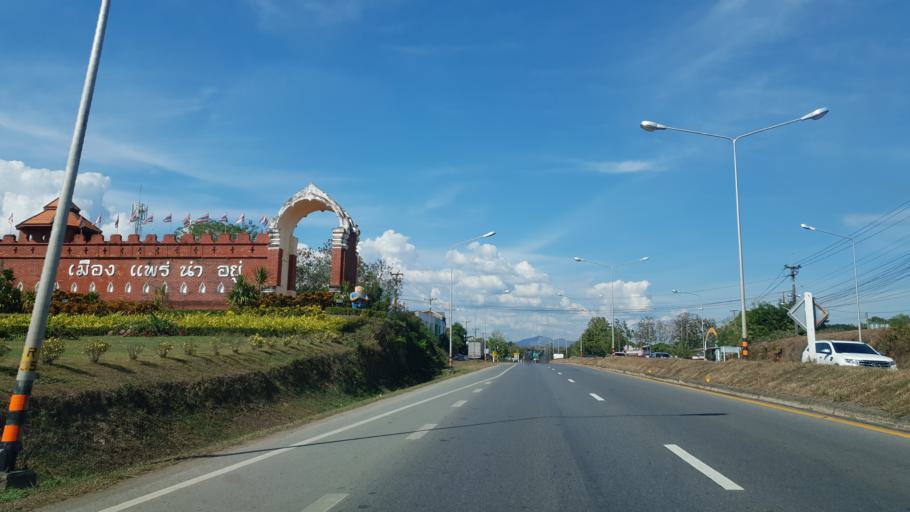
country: TH
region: Phrae
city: Den Chai
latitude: 17.9604
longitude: 100.0672
